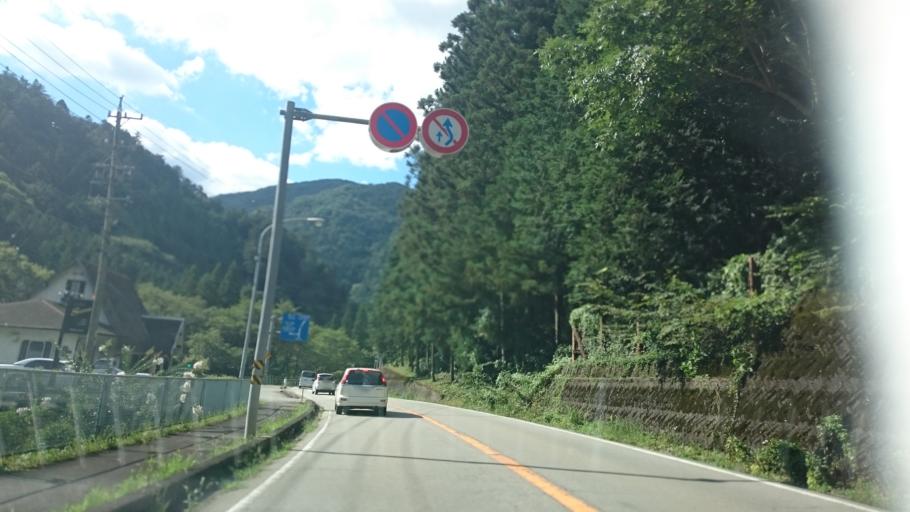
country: JP
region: Gifu
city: Gujo
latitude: 35.7754
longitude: 137.2537
